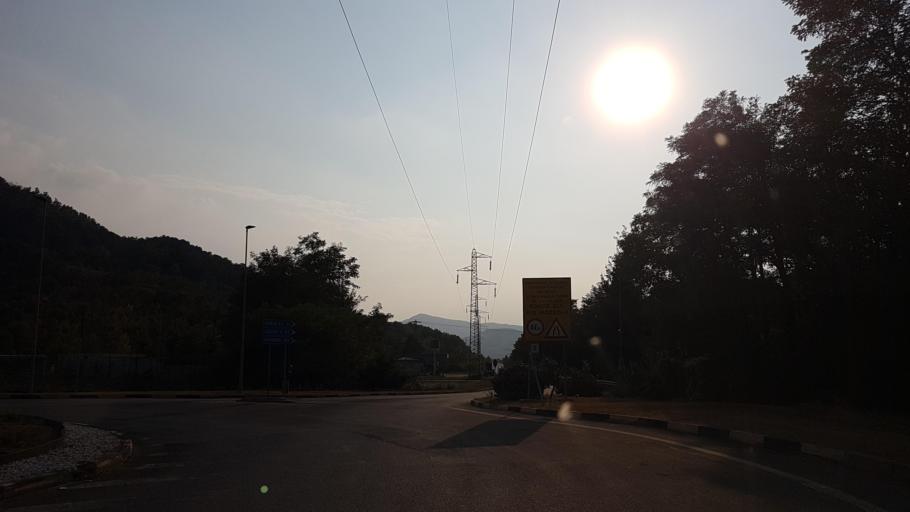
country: IT
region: Emilia-Romagna
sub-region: Provincia di Parma
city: Fornovo di Taro
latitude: 44.6794
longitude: 10.0943
